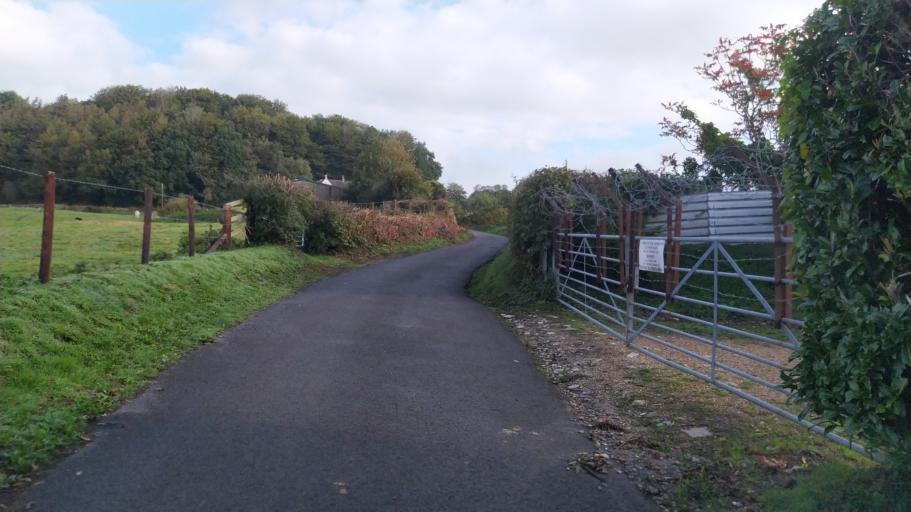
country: GB
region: England
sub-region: Dorset
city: Shaftesbury
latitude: 51.0267
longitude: -2.1345
